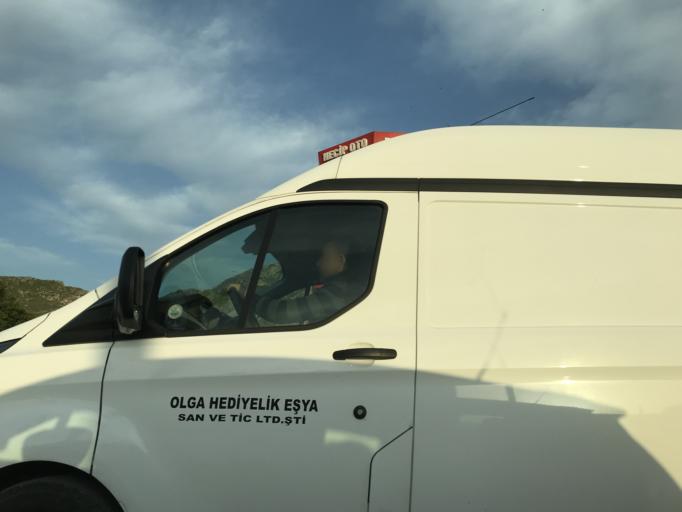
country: TR
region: Hatay
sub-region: Antakya Ilcesi
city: Antakya
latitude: 36.2105
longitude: 36.1663
